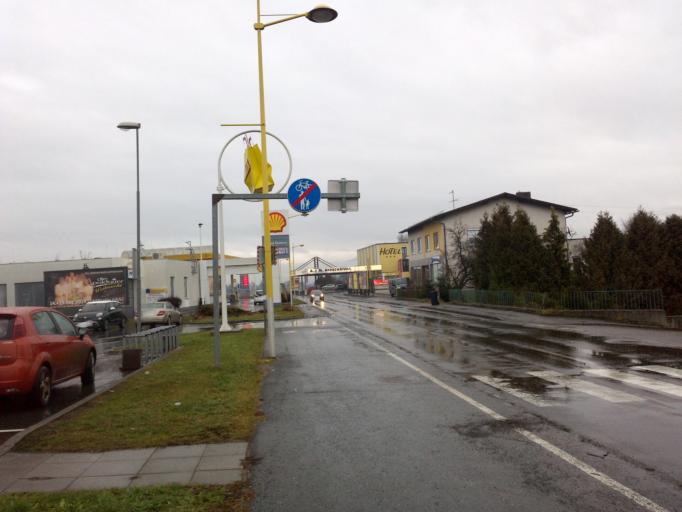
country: AT
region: Styria
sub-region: Politischer Bezirk Murtal
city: Zeltweg
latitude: 47.1970
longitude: 14.7658
